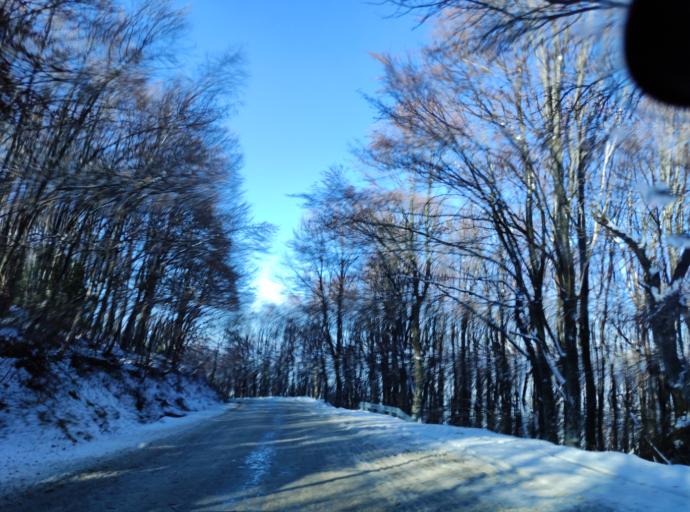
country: BG
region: Sofia-Capital
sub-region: Stolichna Obshtina
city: Sofia
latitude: 42.6054
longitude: 23.3075
